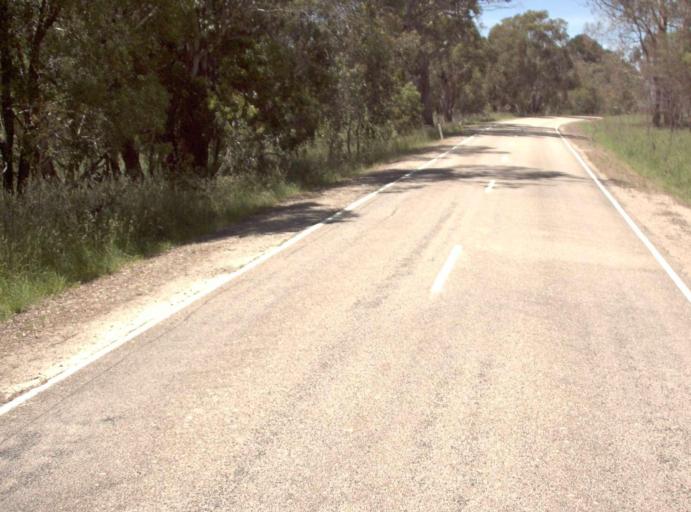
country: AU
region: Victoria
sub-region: East Gippsland
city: Lakes Entrance
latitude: -37.1573
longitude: 148.2583
